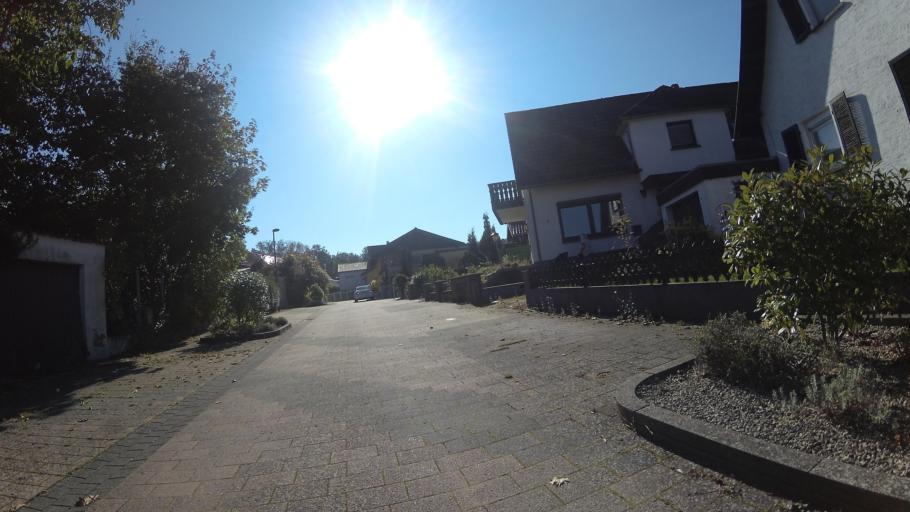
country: DE
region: Rheinland-Pfalz
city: Waldmohr
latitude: 49.3814
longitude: 7.3358
